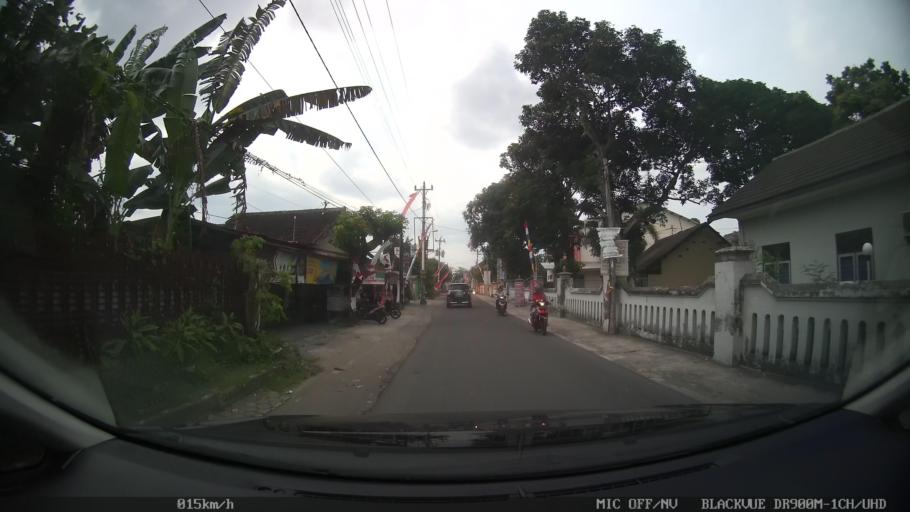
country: ID
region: Daerah Istimewa Yogyakarta
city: Yogyakarta
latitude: -7.7926
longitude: 110.3983
